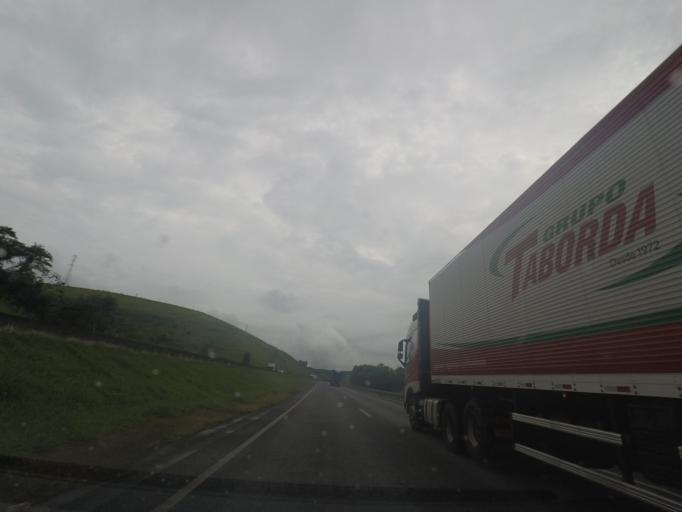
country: BR
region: Sao Paulo
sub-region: Cajati
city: Cajati
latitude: -24.7384
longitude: -48.1225
